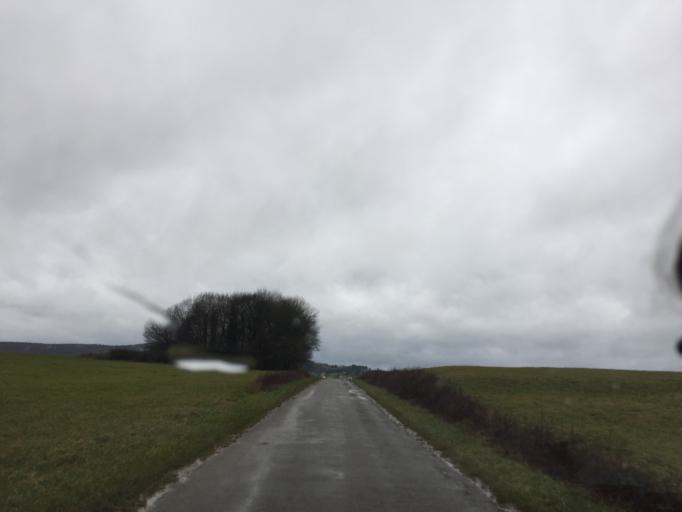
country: FR
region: Franche-Comte
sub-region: Departement du Jura
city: Orchamps
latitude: 47.1970
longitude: 5.6446
